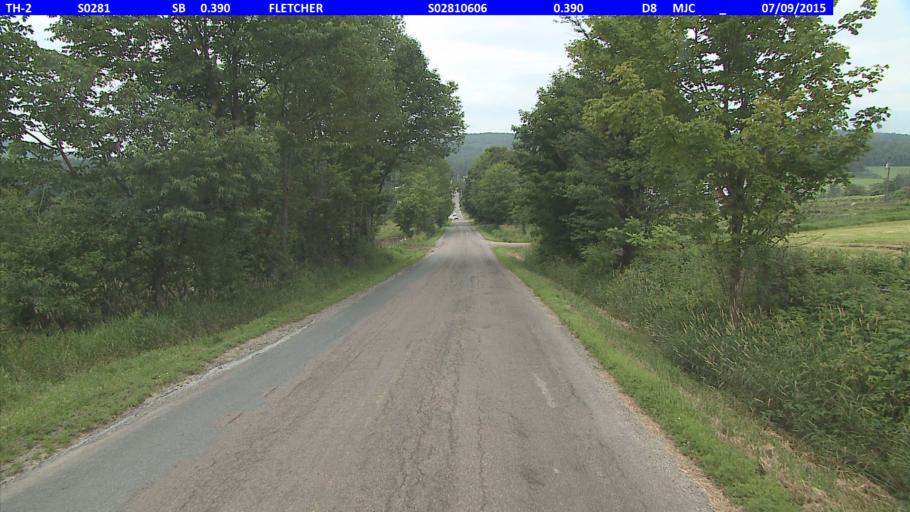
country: US
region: Vermont
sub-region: Chittenden County
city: Milton
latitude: 44.6859
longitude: -72.9213
